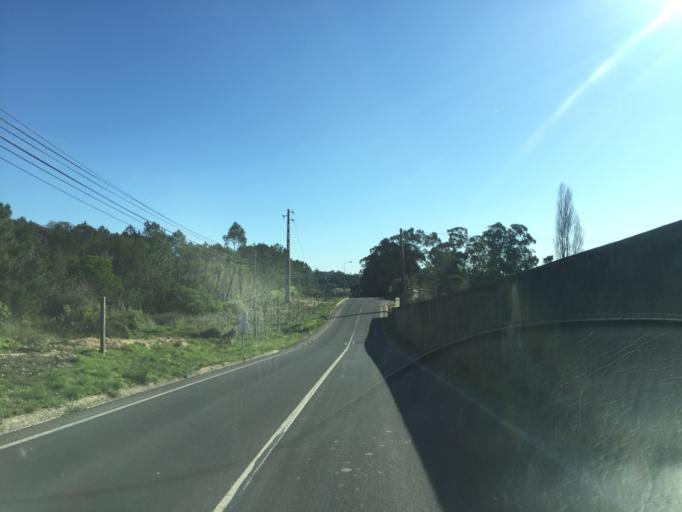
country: PT
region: Lisbon
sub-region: Sintra
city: Belas
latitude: 38.8028
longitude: -9.2846
